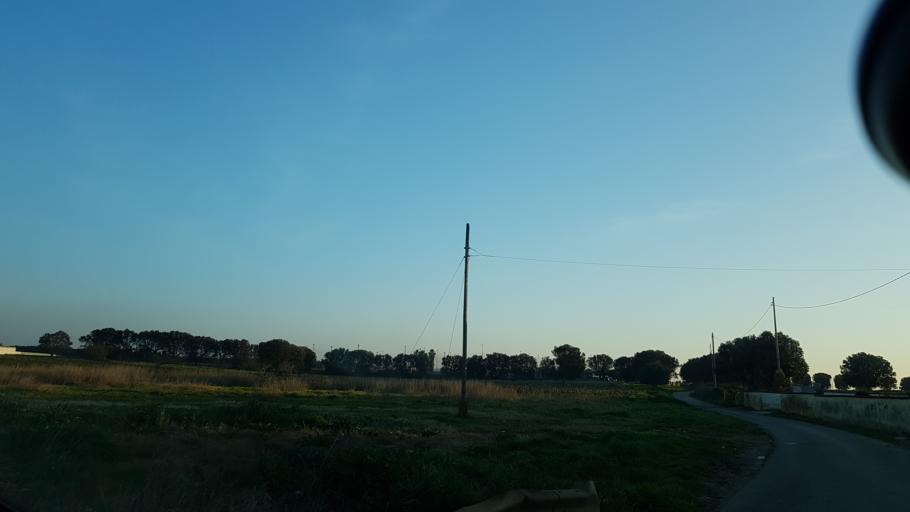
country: IT
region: Apulia
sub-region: Provincia di Brindisi
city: La Rosa
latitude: 40.6135
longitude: 17.9400
